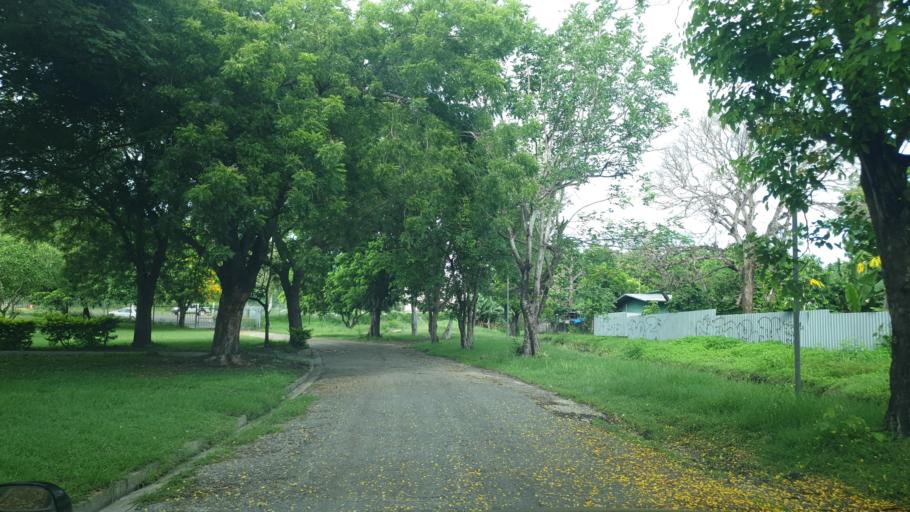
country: PG
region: National Capital
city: Port Moresby
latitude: -9.4560
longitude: 147.1913
